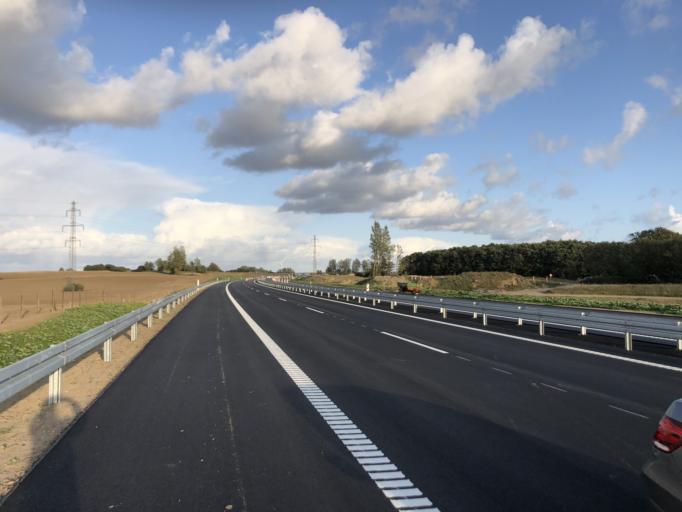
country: DK
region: Zealand
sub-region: Soro Kommune
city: Stenlille
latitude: 55.6615
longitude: 11.6020
